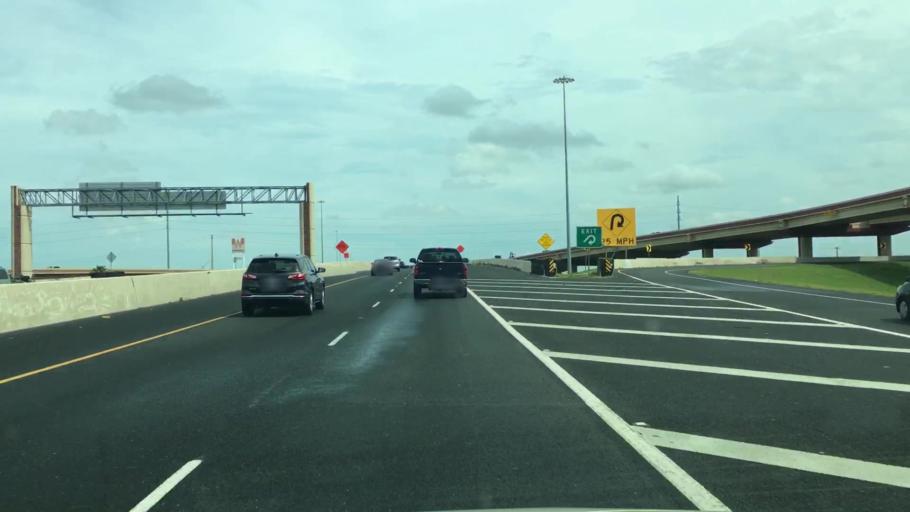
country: US
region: Texas
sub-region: Nueces County
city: Corpus Christi
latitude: 27.7369
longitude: -97.4300
